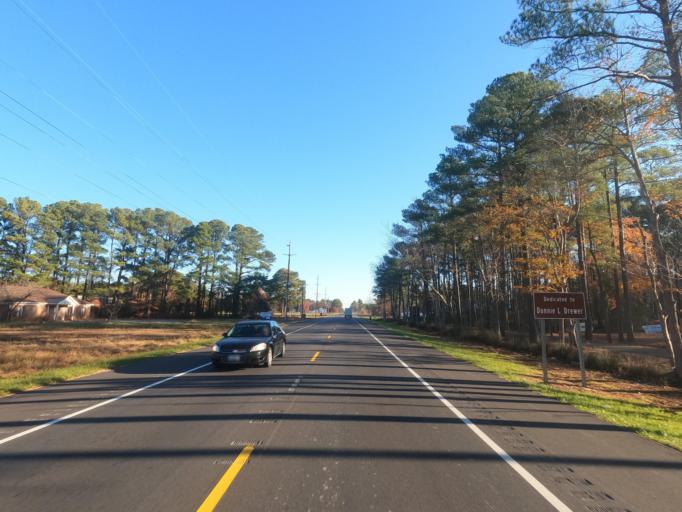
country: US
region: Maryland
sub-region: Somerset County
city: Crisfield
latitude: 38.0024
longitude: -75.8272
